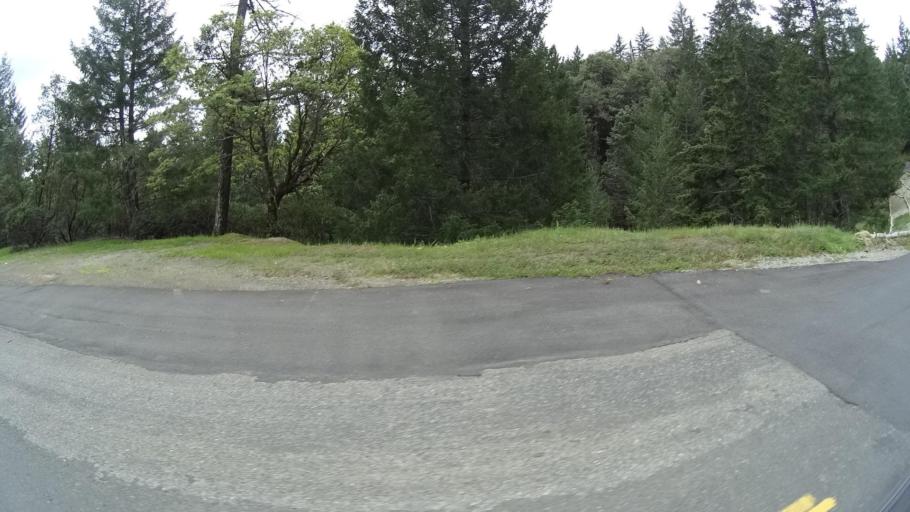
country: US
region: California
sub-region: Humboldt County
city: Redway
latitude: 40.1220
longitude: -123.6662
